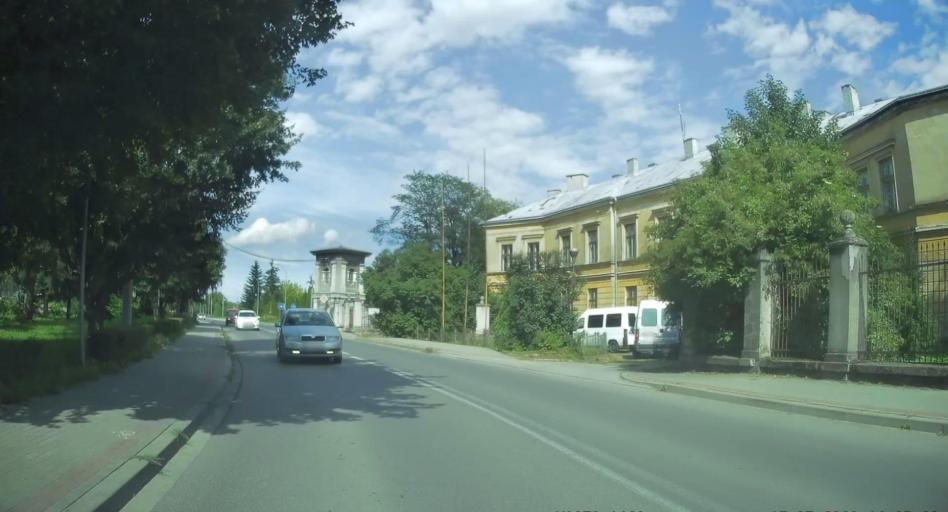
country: PL
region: Subcarpathian Voivodeship
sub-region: Przemysl
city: Przemysl
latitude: 49.7929
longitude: 22.7758
